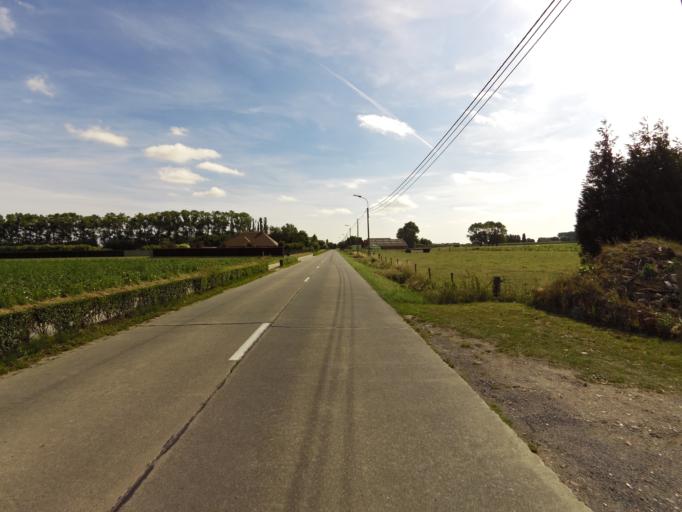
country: BE
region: Flanders
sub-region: Provincie West-Vlaanderen
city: Diksmuide
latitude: 50.9577
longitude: 2.8711
